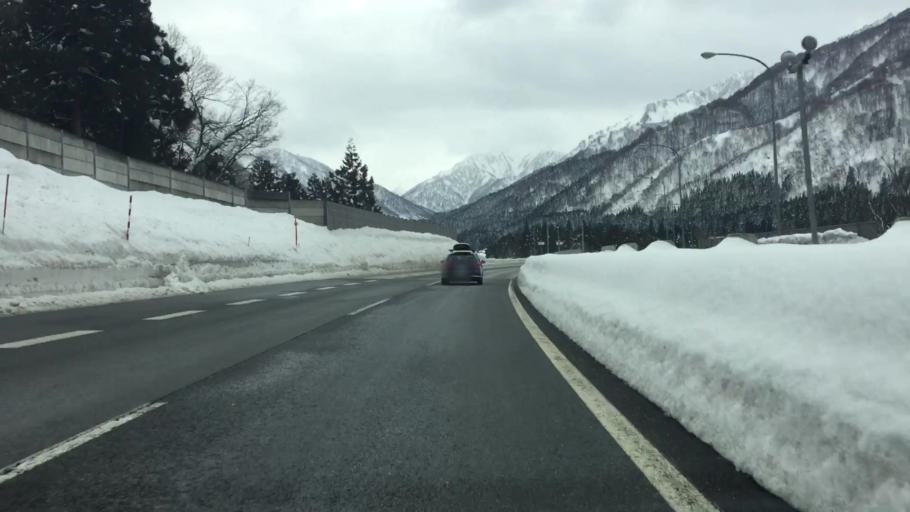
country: JP
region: Niigata
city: Shiozawa
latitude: 36.9025
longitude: 138.8478
